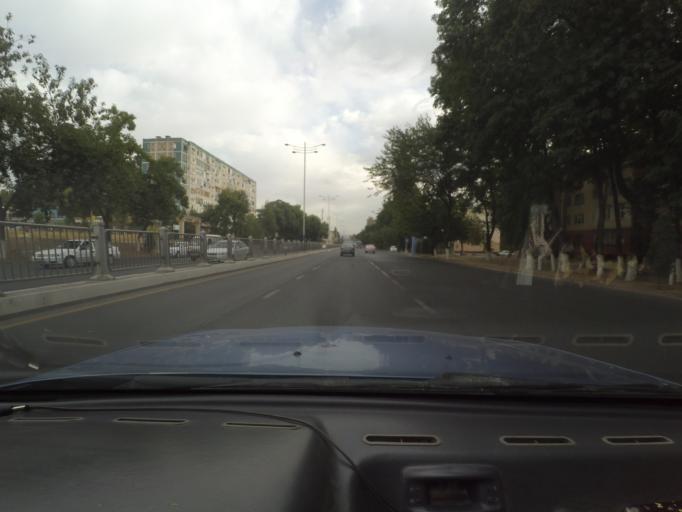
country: UZ
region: Toshkent
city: Salor
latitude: 41.3612
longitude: 69.3910
